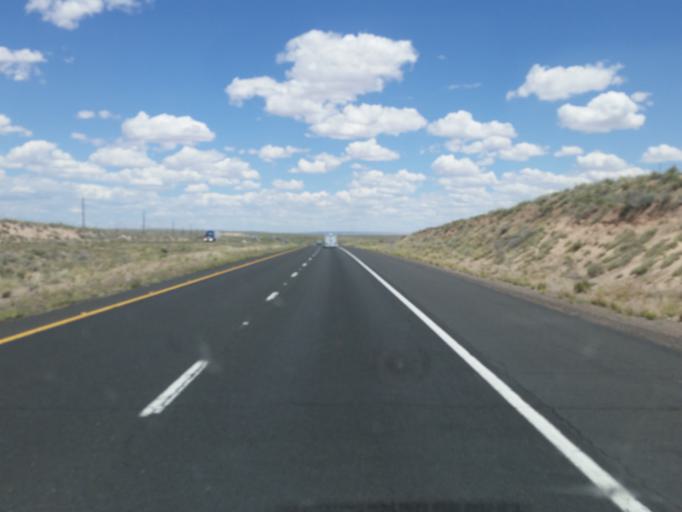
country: US
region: Arizona
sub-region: Navajo County
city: Holbrook
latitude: 34.9906
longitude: -109.9732
